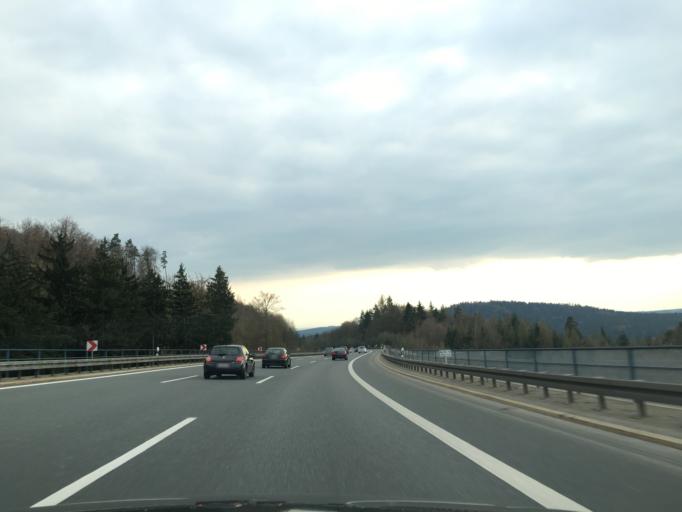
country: DE
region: Bavaria
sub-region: Regierungsbezirk Mittelfranken
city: Simmelsdorf
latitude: 49.5927
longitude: 11.3495
